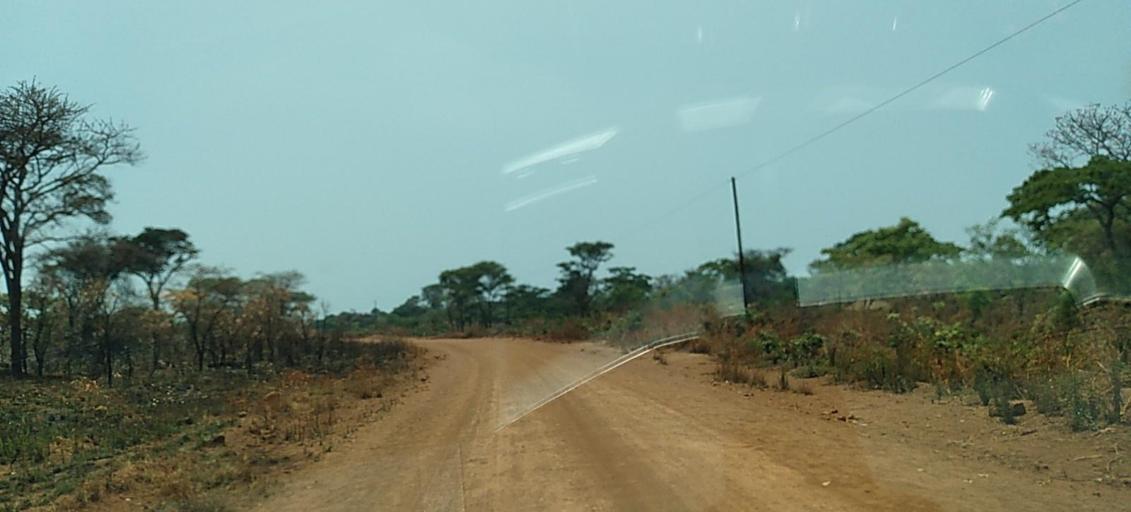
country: CD
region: Katanga
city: Kipushi
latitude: -11.9354
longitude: 26.9663
